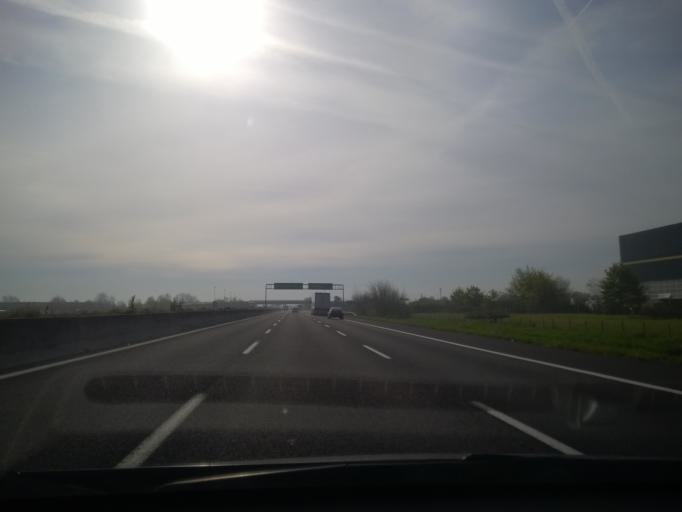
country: IT
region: Emilia-Romagna
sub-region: Provincia di Ravenna
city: Faenza
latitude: 44.3258
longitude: 11.8998
